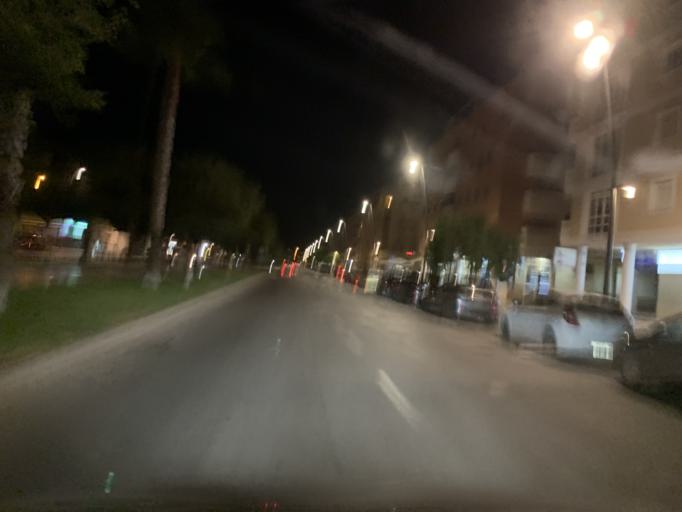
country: ES
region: Andalusia
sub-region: Provincia de Almeria
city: Roquetas de Mar
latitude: 36.7756
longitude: -2.6086
